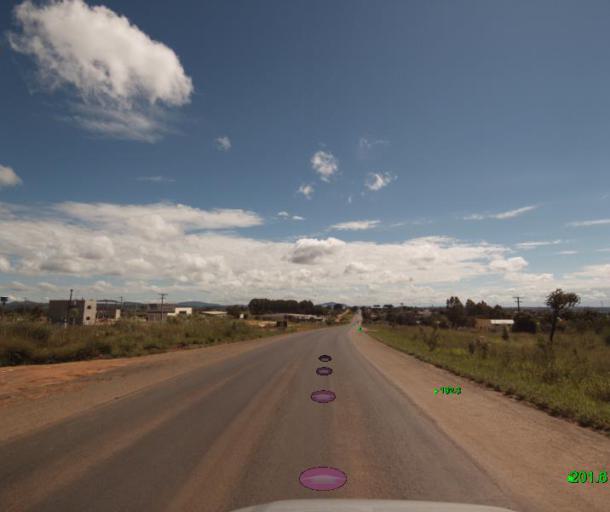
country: BR
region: Goias
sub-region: Uruacu
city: Uruacu
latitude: -14.5393
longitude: -49.1622
